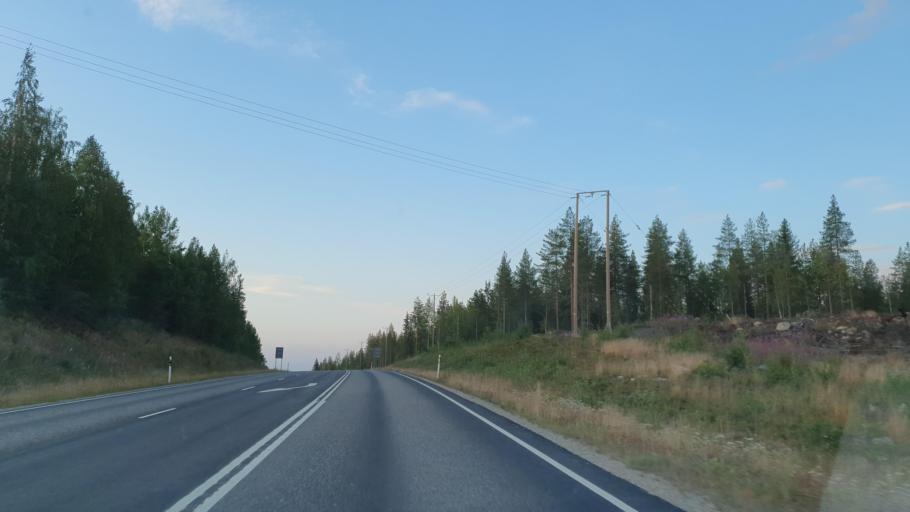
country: FI
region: Kainuu
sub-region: Kehys-Kainuu
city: Hyrynsalmi
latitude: 64.6900
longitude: 28.5548
